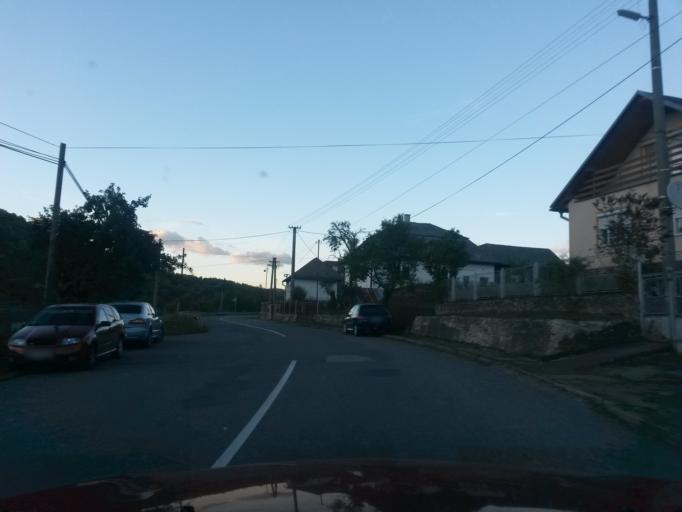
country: UA
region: Zakarpattia
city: Velykyi Bereznyi
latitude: 48.8565
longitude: 22.3537
